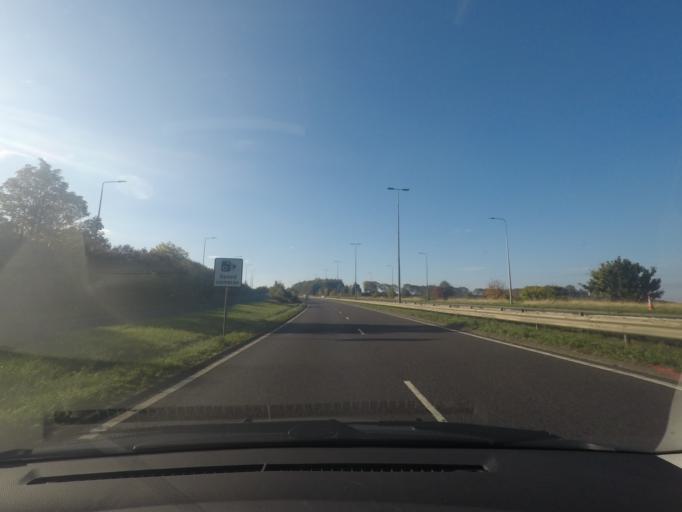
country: GB
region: England
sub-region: North Lincolnshire
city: Barton upon Humber
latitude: 53.6885
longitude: -0.4546
